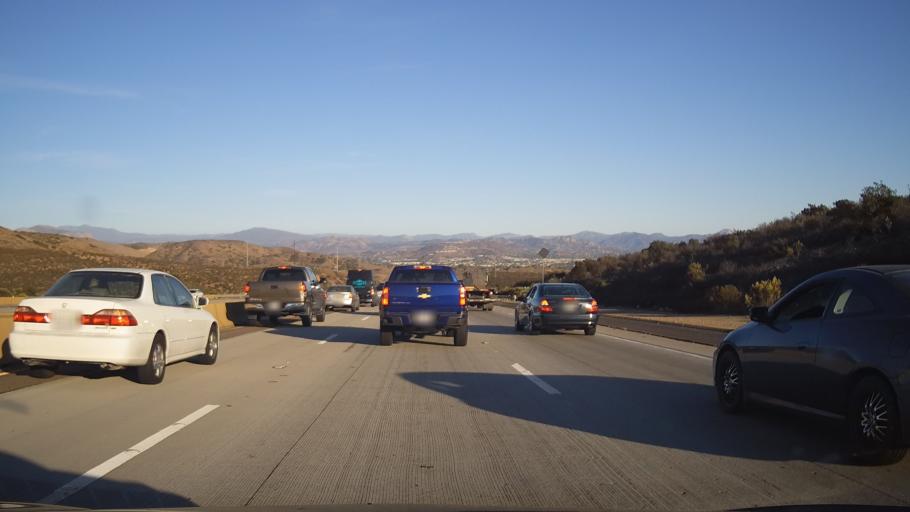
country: US
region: California
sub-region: San Diego County
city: Santee
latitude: 32.8535
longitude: -117.0535
